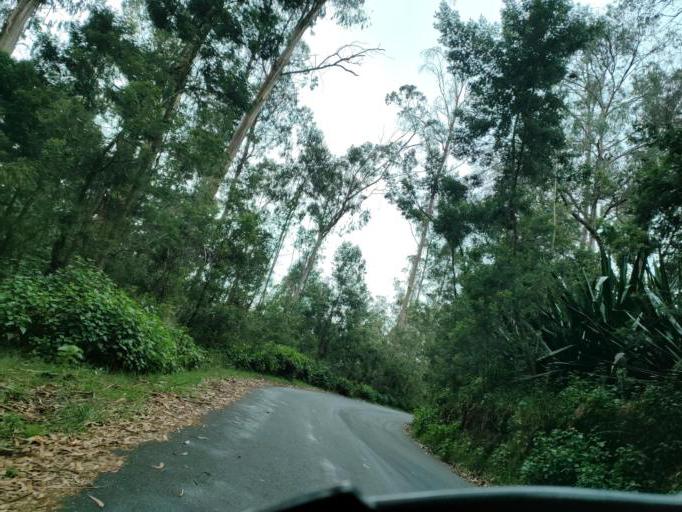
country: IN
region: Tamil Nadu
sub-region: Dindigul
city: Kodaikanal
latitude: 10.2433
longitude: 77.3688
